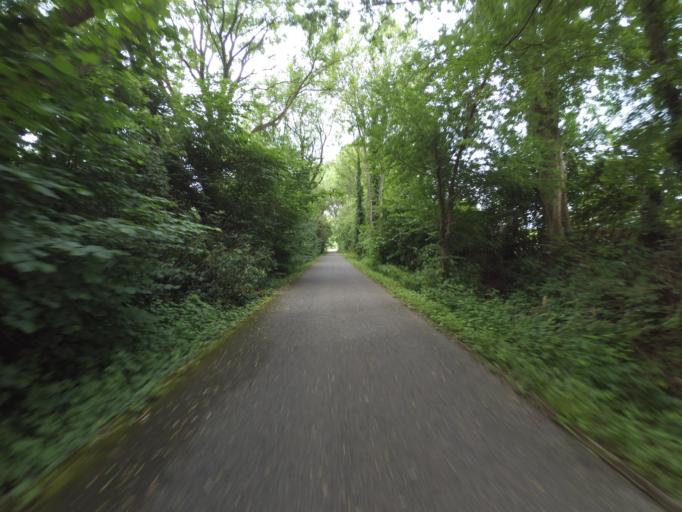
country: DE
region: North Rhine-Westphalia
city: Stolberg
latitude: 50.7267
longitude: 6.1819
